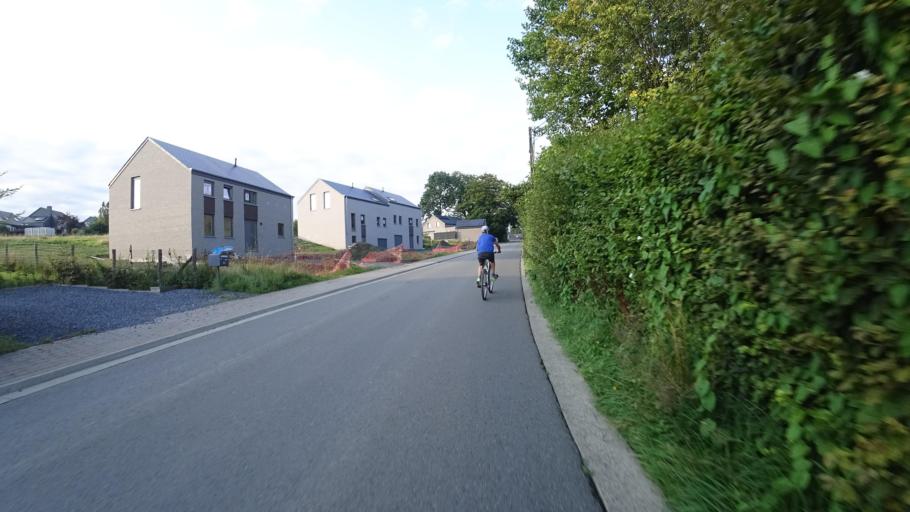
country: BE
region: Wallonia
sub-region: Province du Luxembourg
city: Neufchateau
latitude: 49.9023
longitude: 5.3863
